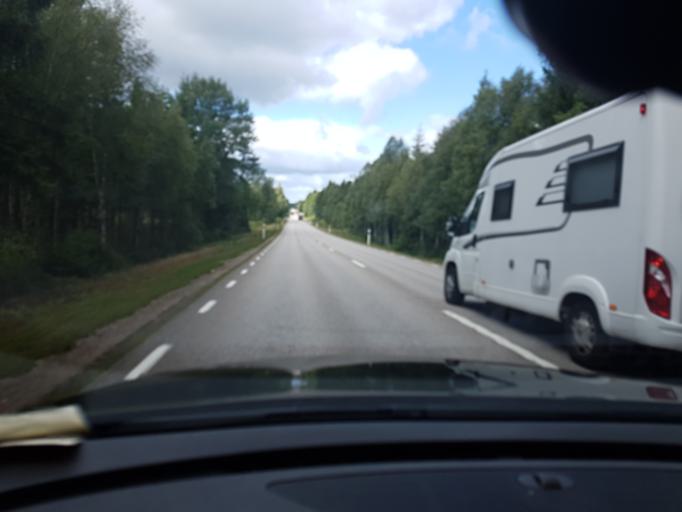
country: SE
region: Kronoberg
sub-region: Lessebo Kommun
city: Lessebo
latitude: 56.7298
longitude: 15.3386
